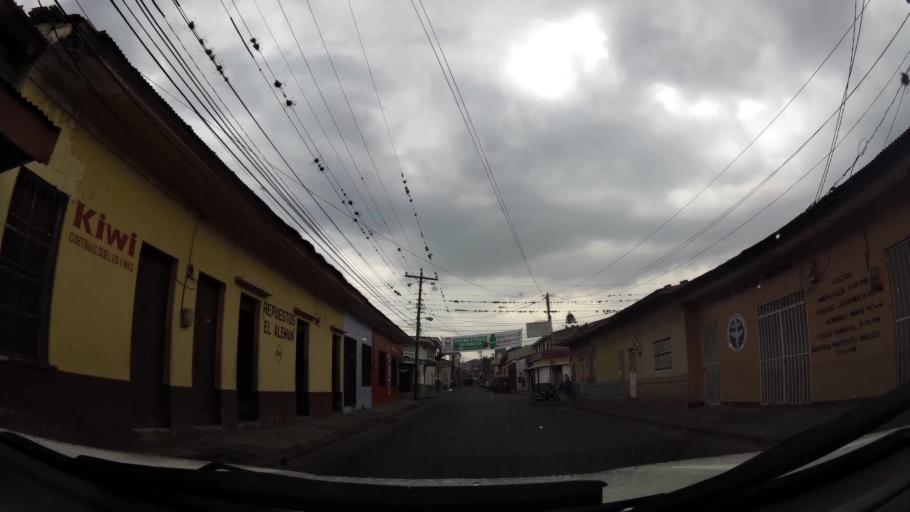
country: NI
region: Jinotega
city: Jinotega
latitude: 13.0954
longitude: -86.0026
